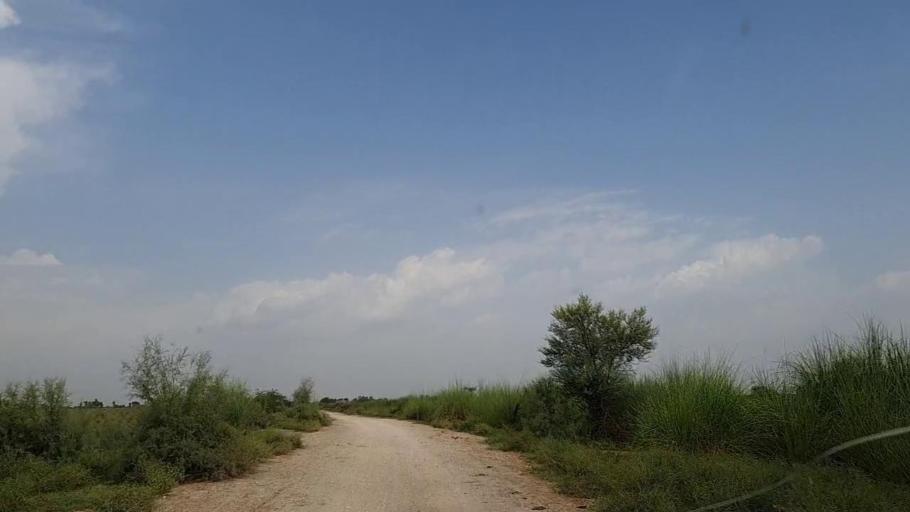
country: PK
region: Sindh
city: Khanpur
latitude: 27.8211
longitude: 69.5260
